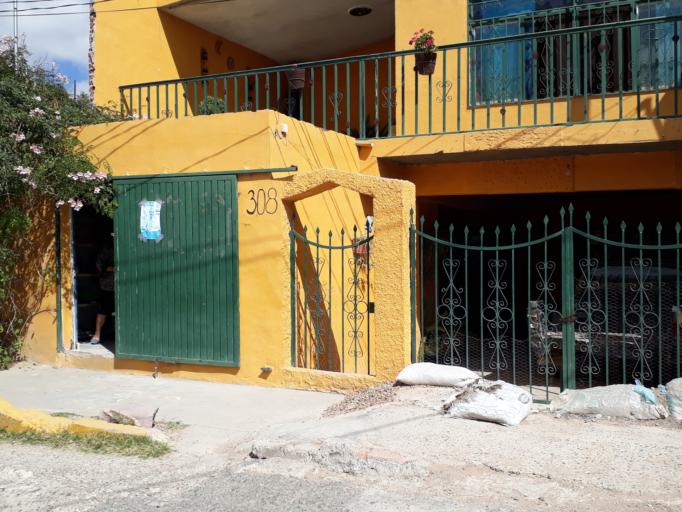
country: MX
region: Aguascalientes
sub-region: Aguascalientes
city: San Sebastian [Fraccionamiento]
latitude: 21.8003
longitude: -102.2737
